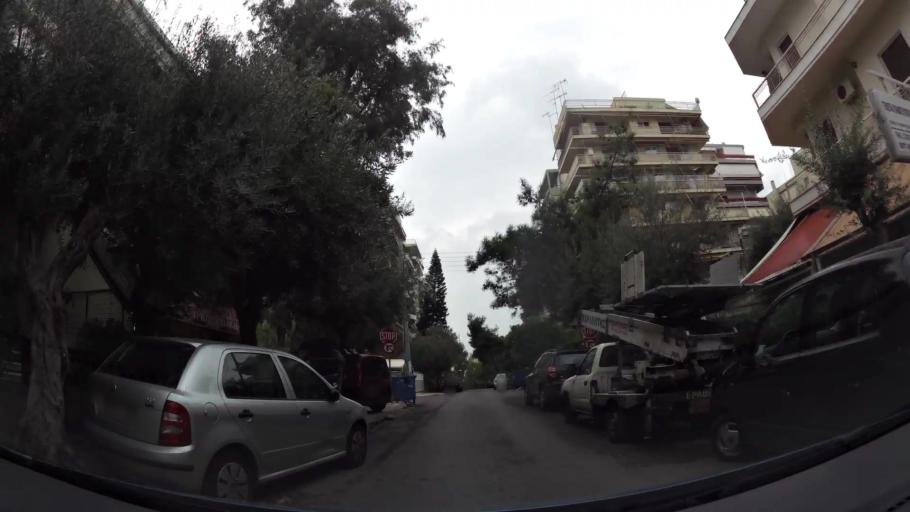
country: GR
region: Attica
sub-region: Nomarchia Athinas
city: Palaio Faliro
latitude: 37.9223
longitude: 23.7031
